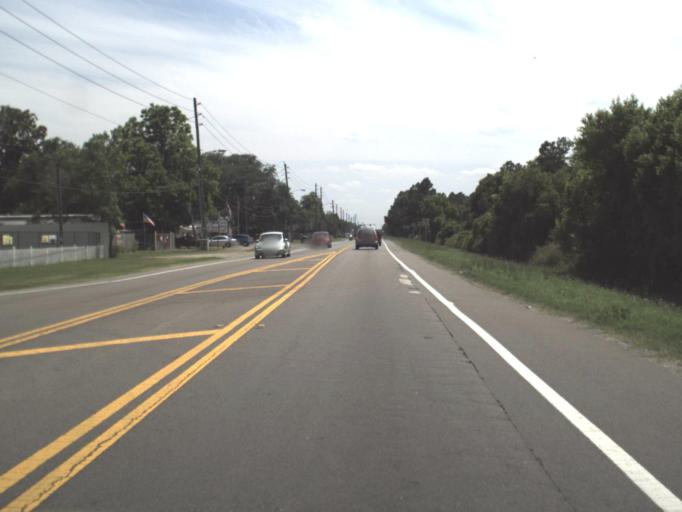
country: US
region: Florida
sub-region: Duval County
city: Jacksonville
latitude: 30.4721
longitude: -81.6311
